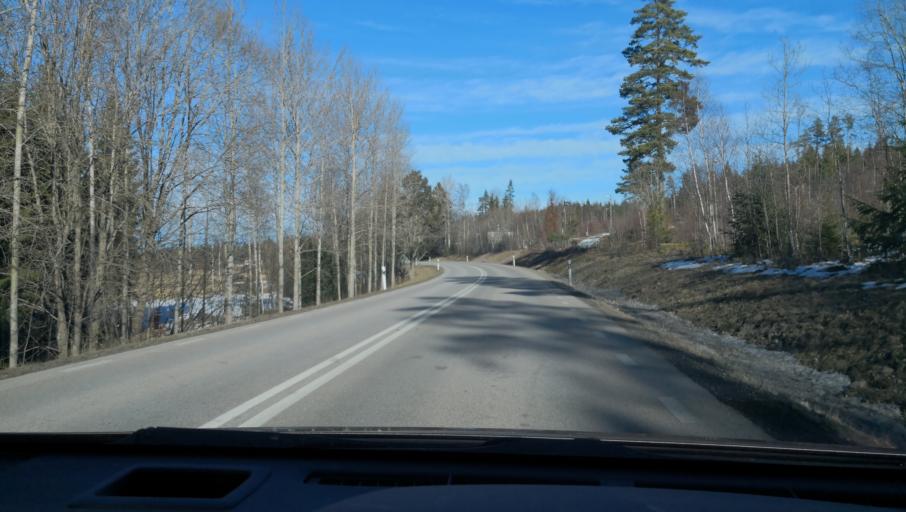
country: SE
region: Uppsala
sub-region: Uppsala Kommun
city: Vattholma
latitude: 60.0749
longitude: 17.7599
